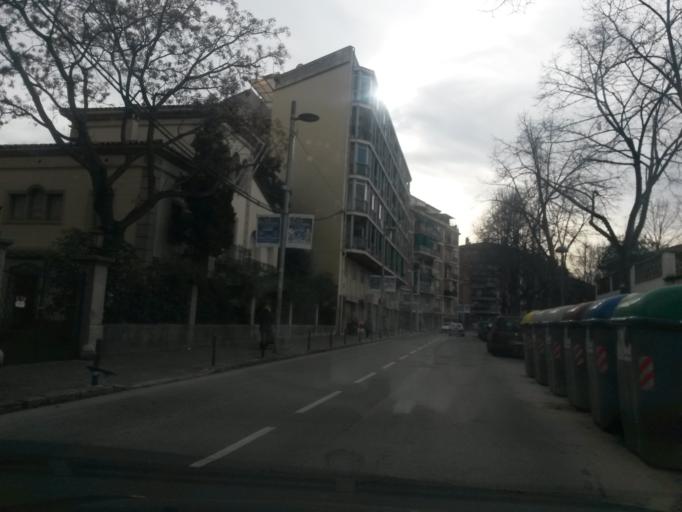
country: ES
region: Catalonia
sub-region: Provincia de Girona
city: Girona
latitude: 41.9759
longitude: 2.8133
